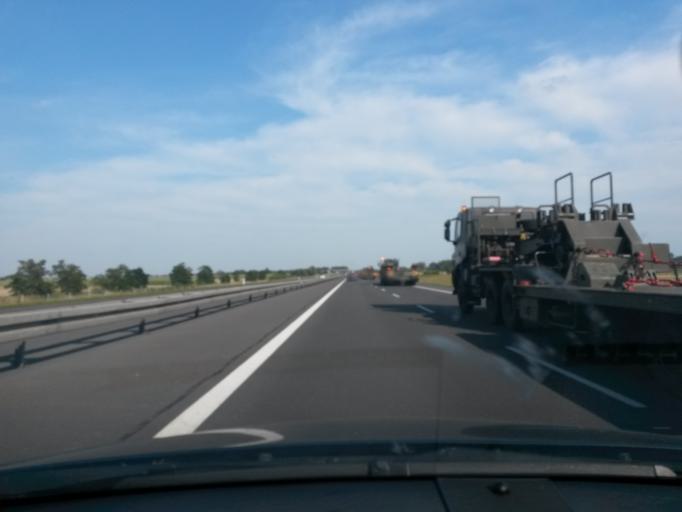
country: PL
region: Greater Poland Voivodeship
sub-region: Powiat wrzesinski
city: Wrzesnia
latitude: 52.2980
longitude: 17.6369
